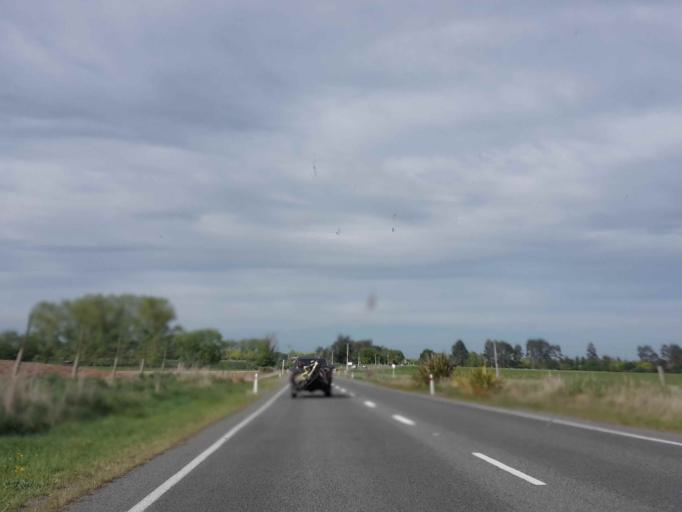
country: NZ
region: Canterbury
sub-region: Timaru District
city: Pleasant Point
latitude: -44.1203
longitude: 171.1961
